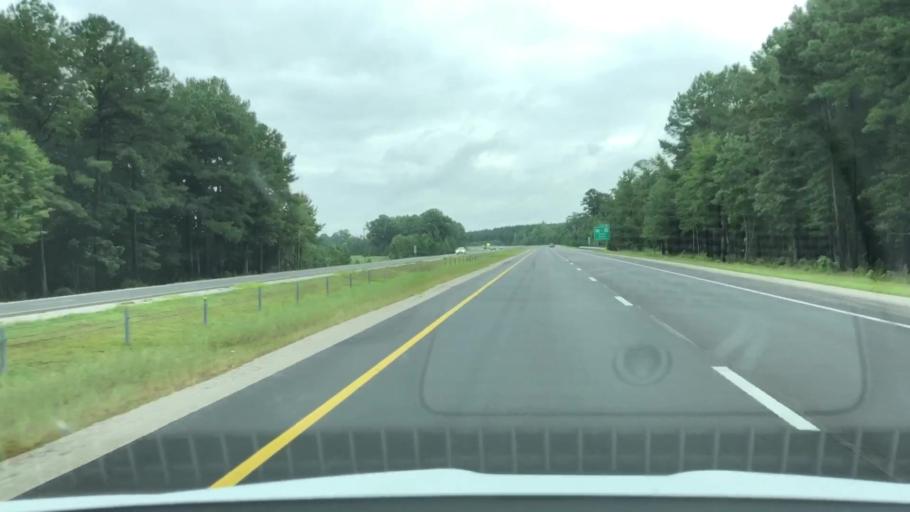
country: US
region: North Carolina
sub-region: Wilson County
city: Lucama
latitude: 35.6554
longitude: -77.9585
